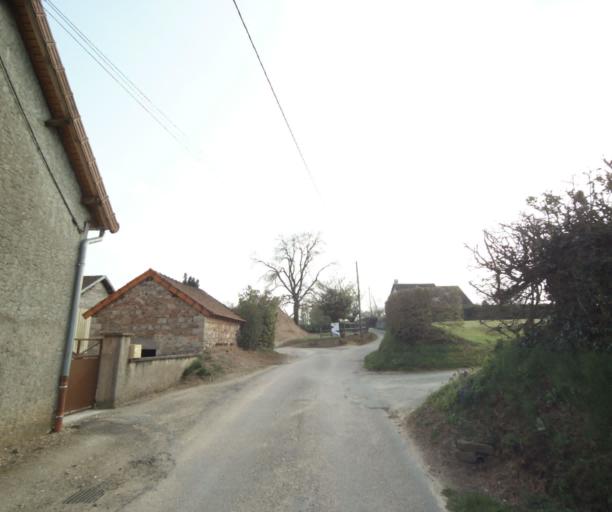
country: FR
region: Bourgogne
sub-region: Departement de Saone-et-Loire
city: Charolles
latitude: 46.4652
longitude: 4.4309
